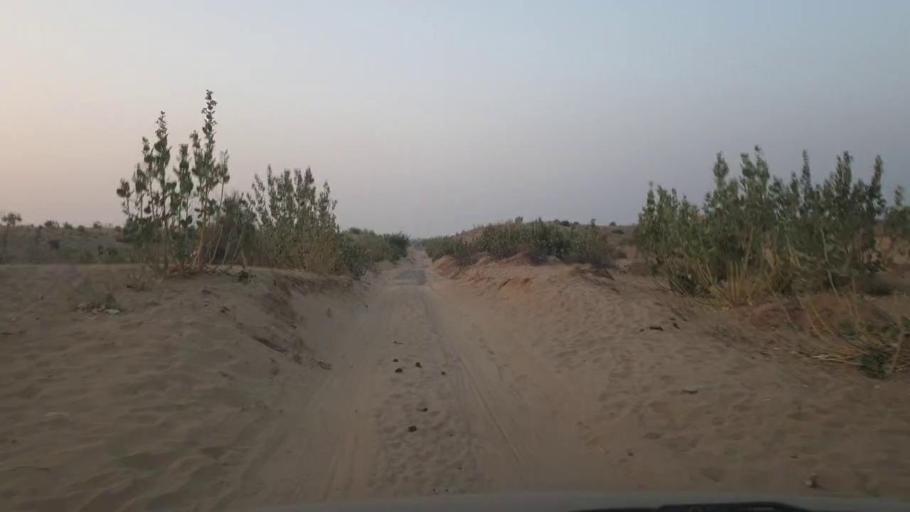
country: PK
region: Sindh
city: Umarkot
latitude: 25.2969
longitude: 70.0751
